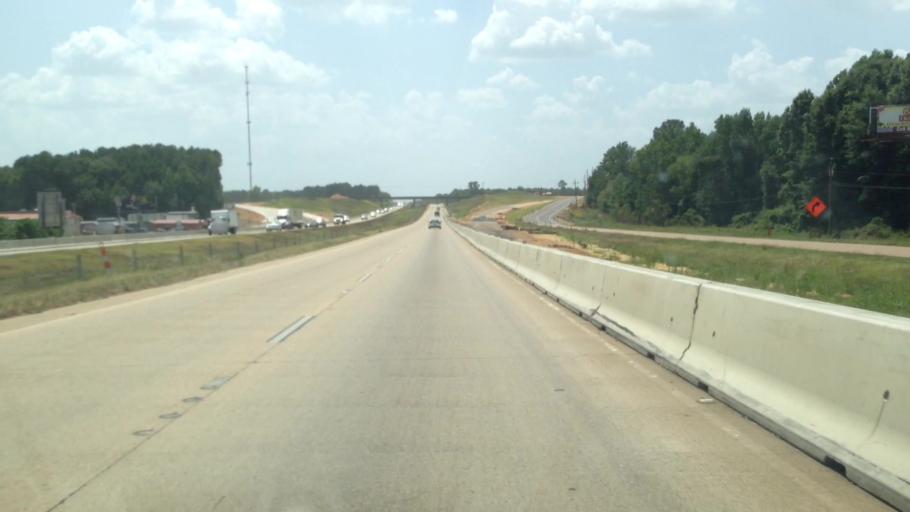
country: US
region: Louisiana
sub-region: Lincoln Parish
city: Ruston
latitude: 32.5405
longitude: -92.6704
